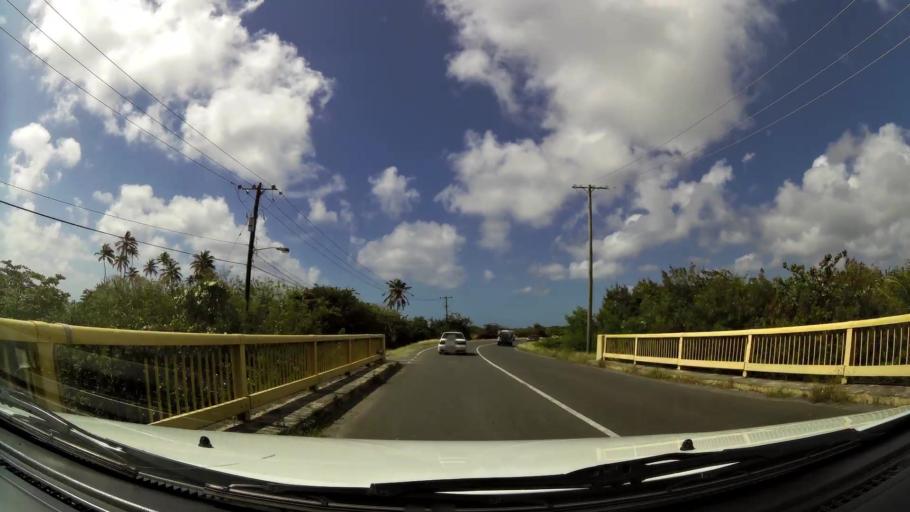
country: LC
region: Vieux-Fort
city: Vieux Fort
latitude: 13.7312
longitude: -60.9687
